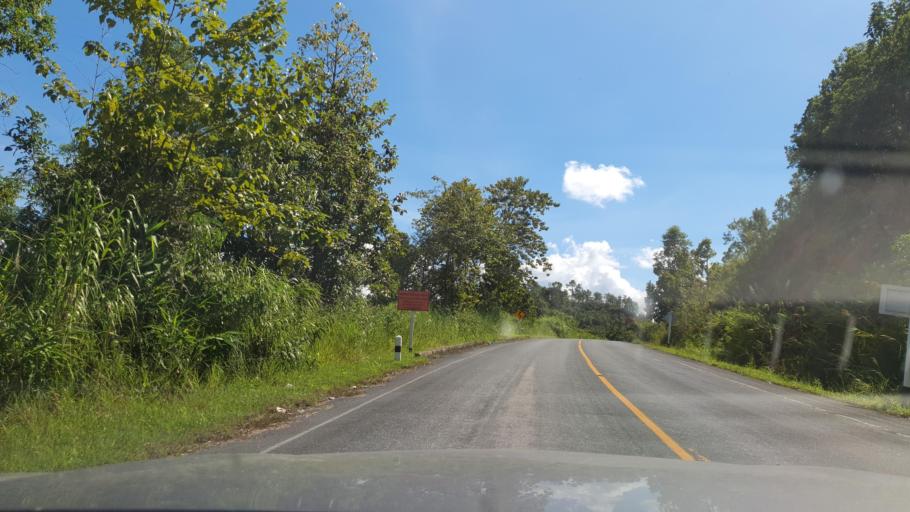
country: TH
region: Chiang Mai
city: Phrao
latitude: 19.3542
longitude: 99.2763
